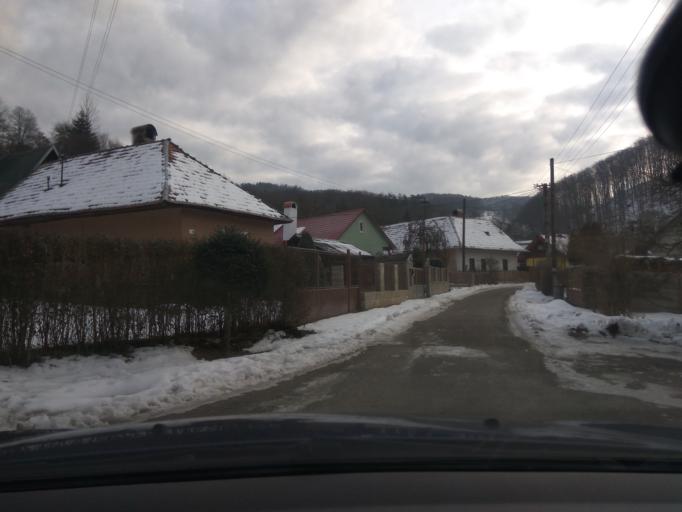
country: SK
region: Banskobystricky
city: Zarnovica
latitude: 48.4809
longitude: 18.7535
